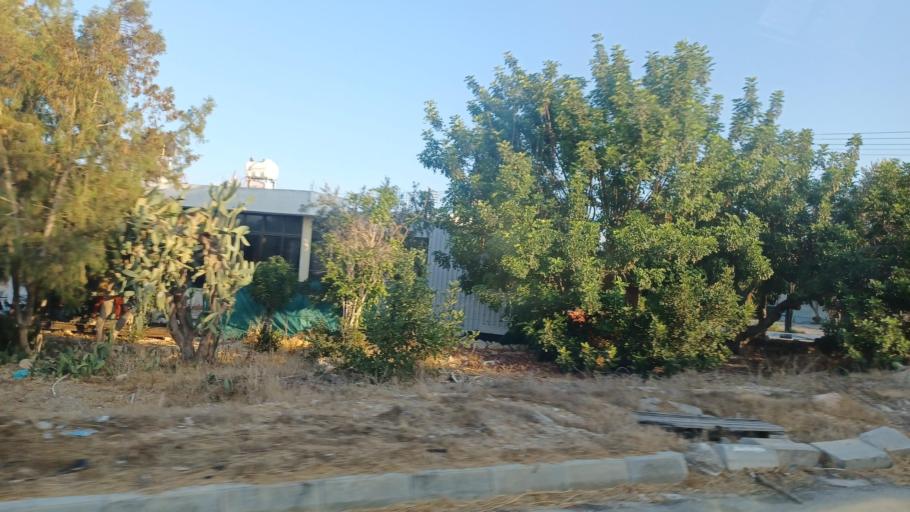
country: CY
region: Pafos
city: Paphos
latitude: 34.7859
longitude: 32.4515
